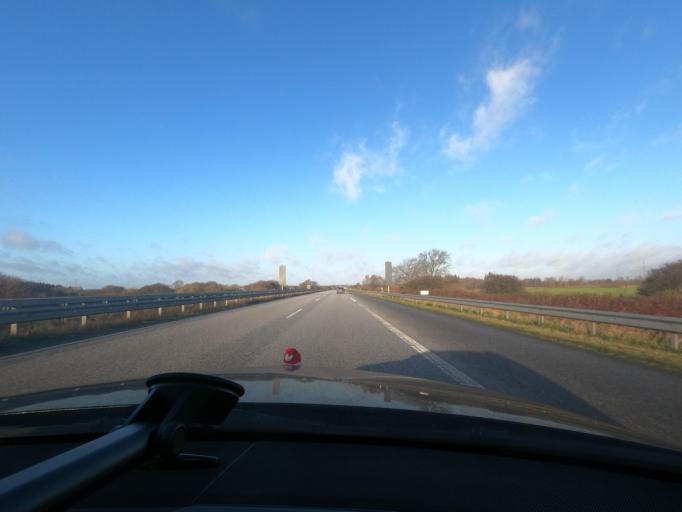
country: DE
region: Schleswig-Holstein
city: Bollingstedt
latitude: 54.6183
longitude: 9.4429
